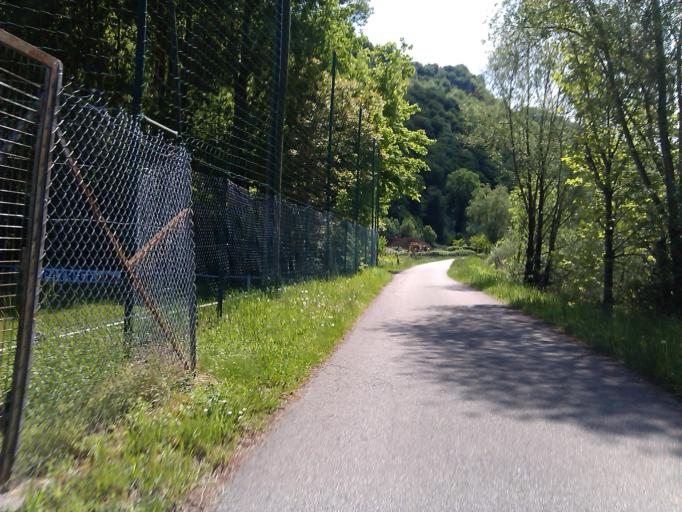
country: FR
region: Franche-Comte
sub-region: Departement du Doubs
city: Beure
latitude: 47.2037
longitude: 5.9944
